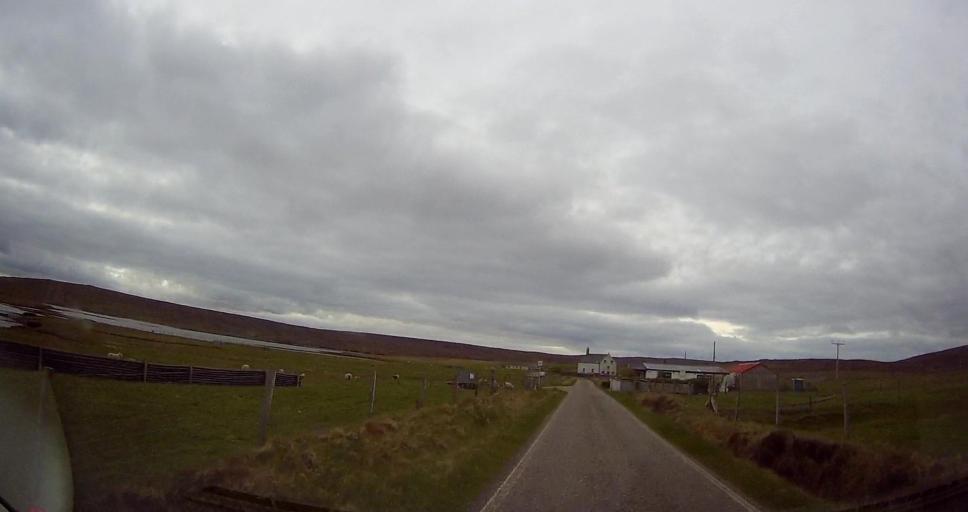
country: GB
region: Scotland
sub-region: Shetland Islands
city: Shetland
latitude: 60.5026
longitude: -1.0970
